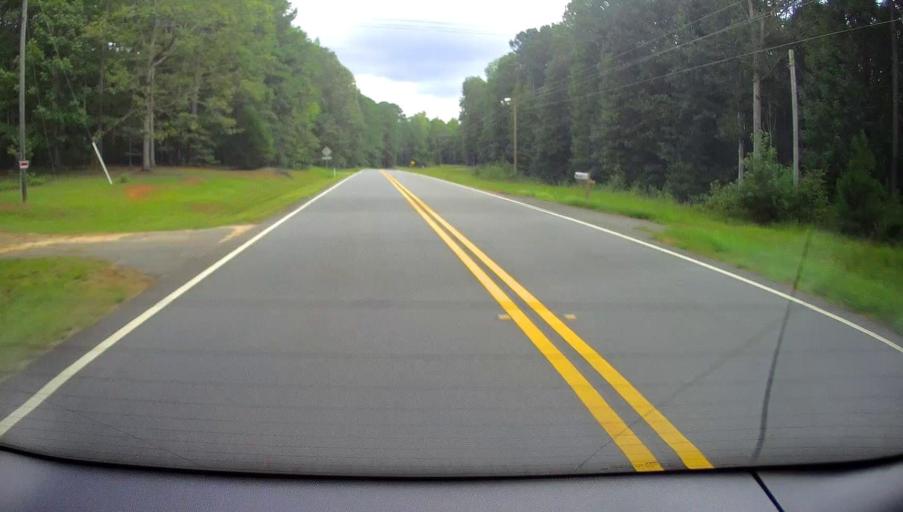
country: US
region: Georgia
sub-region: Monroe County
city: Forsyth
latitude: 32.8845
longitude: -83.9675
